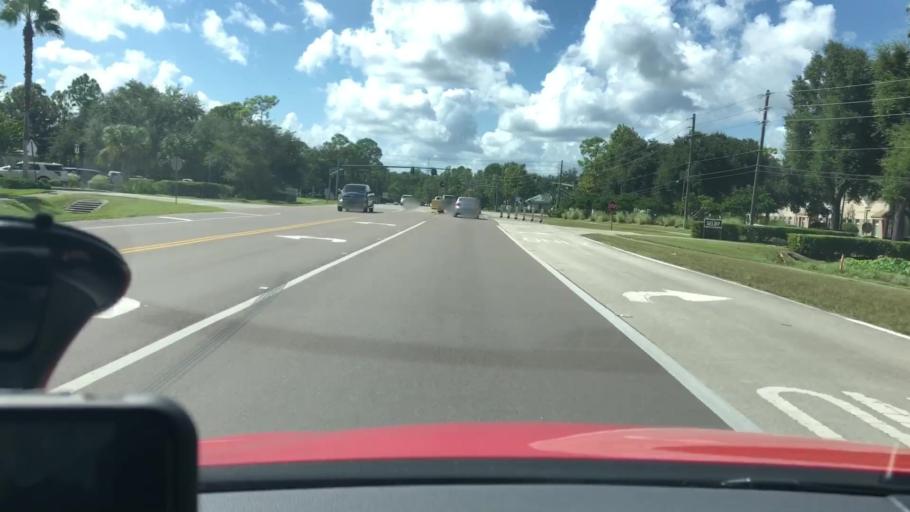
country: US
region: Florida
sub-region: Volusia County
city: Ormond Beach
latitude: 29.2618
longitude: -81.0922
